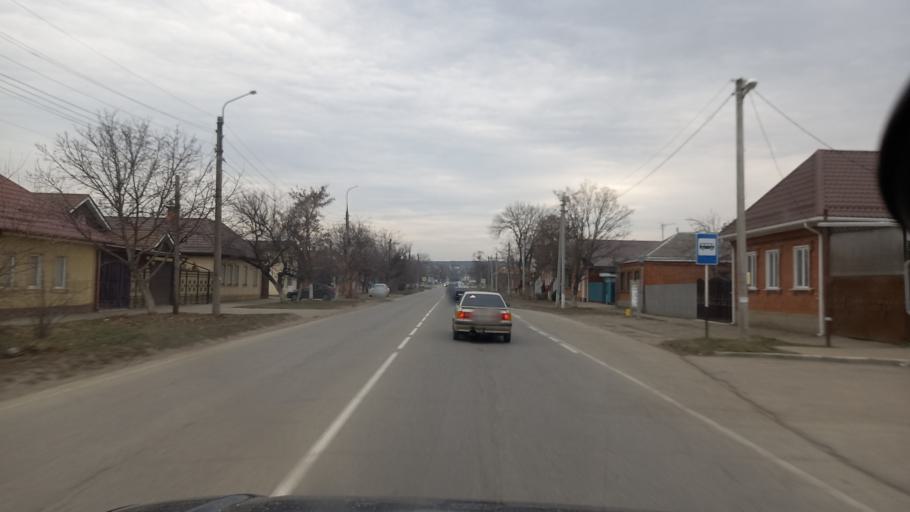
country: RU
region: Adygeya
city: Maykop
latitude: 44.5985
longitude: 40.1286
